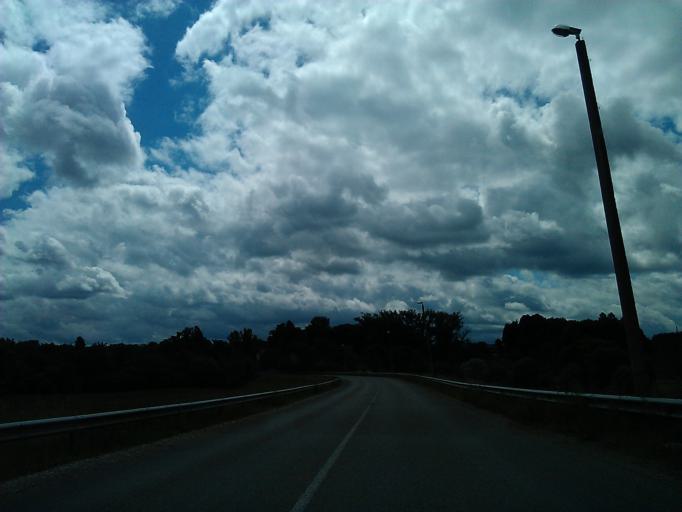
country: LV
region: Talsu Rajons
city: Stende
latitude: 57.0733
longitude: 22.2914
